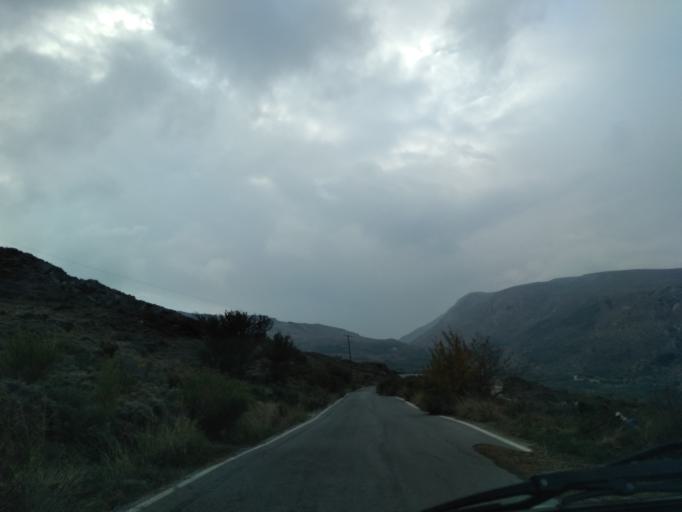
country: GR
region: Crete
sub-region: Nomos Lasithiou
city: Siteia
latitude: 35.1419
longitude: 26.0234
